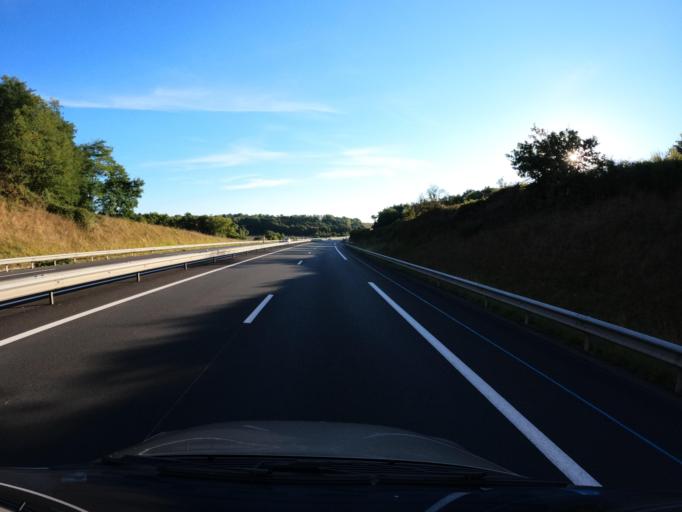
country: FR
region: Pays de la Loire
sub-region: Departement de la Vendee
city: Saint-Laurent-sur-Sevre
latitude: 46.9693
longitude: -0.9190
